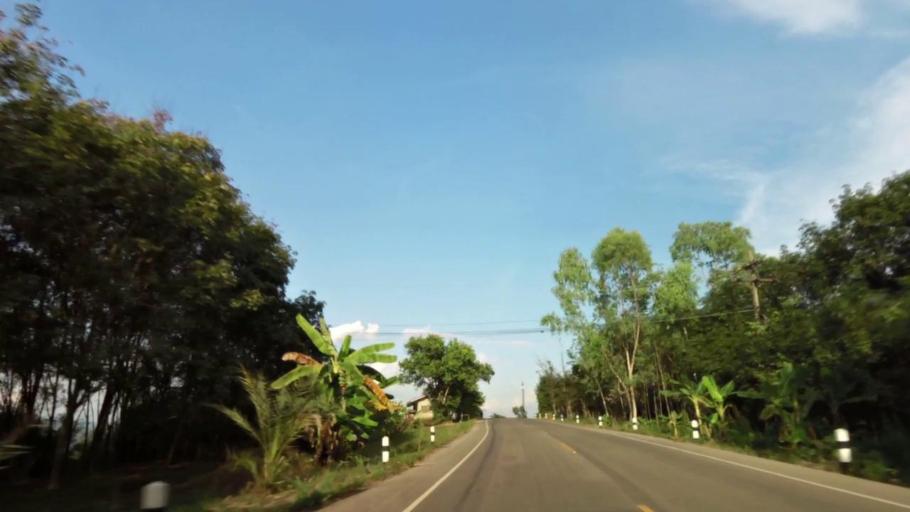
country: TH
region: Chiang Rai
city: Khun Tan
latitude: 19.8570
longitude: 100.3878
